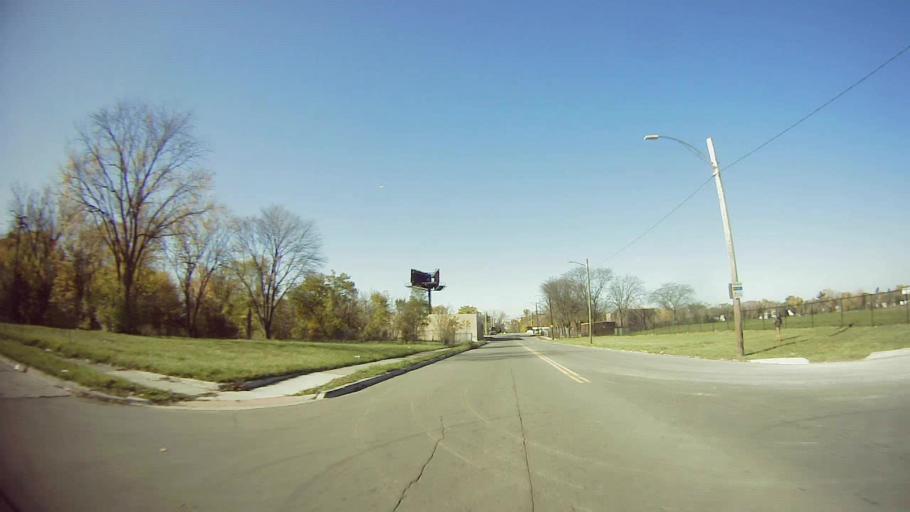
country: US
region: Michigan
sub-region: Wayne County
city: Dearborn
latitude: 42.3507
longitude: -83.2140
